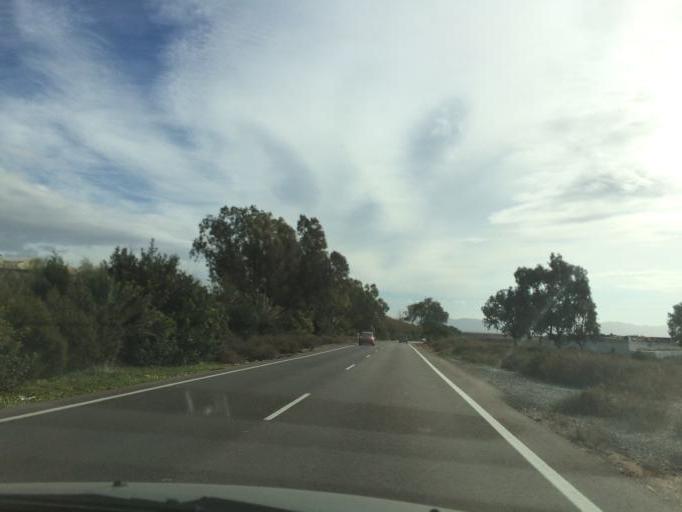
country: ES
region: Andalusia
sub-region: Provincia de Almeria
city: Retamar
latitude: 36.8372
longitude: -2.2897
